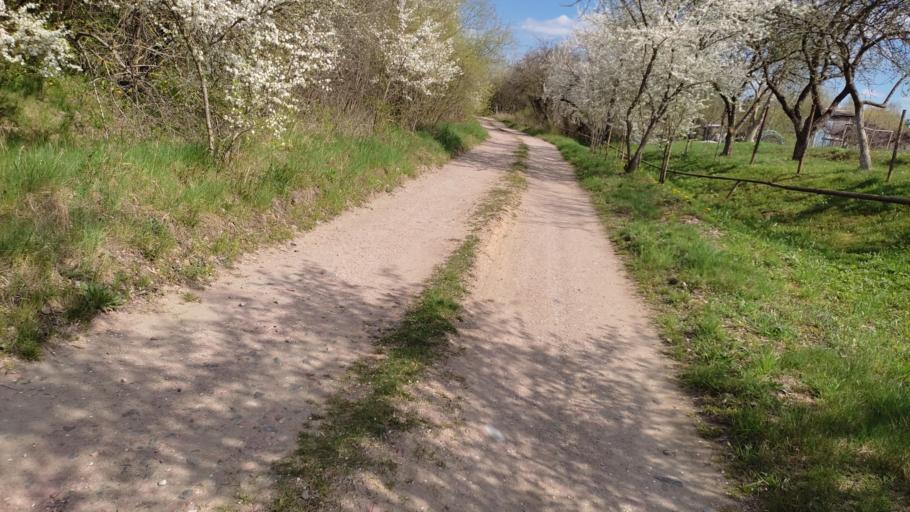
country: BY
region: Grodnenskaya
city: Hrodna
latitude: 53.6569
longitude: 23.8987
